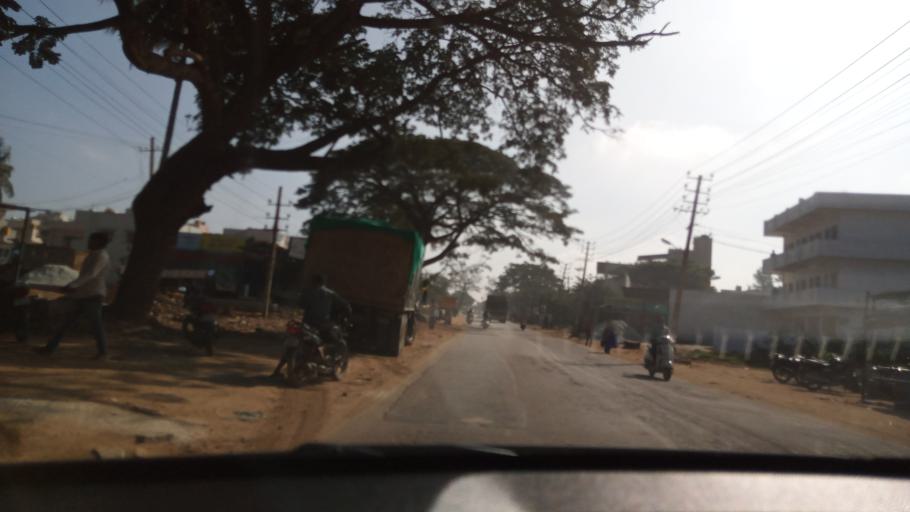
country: IN
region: Karnataka
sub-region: Bangalore Rural
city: Devanhalli
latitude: 13.2572
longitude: 77.7154
